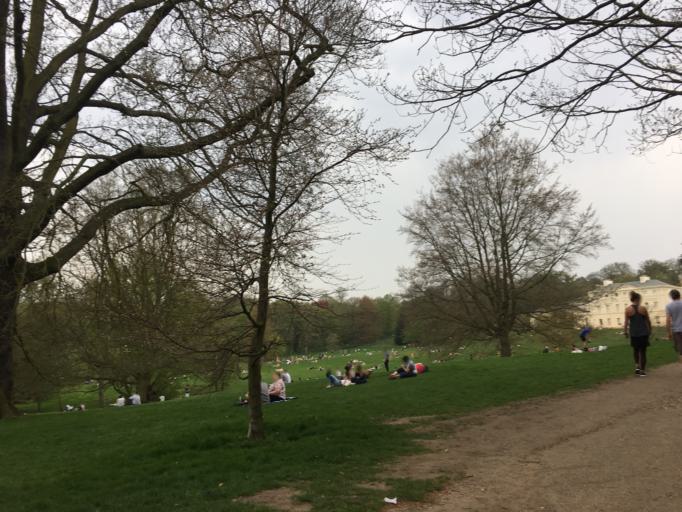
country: GB
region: England
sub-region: Greater London
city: Belsize Park
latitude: 51.5702
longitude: -0.1653
